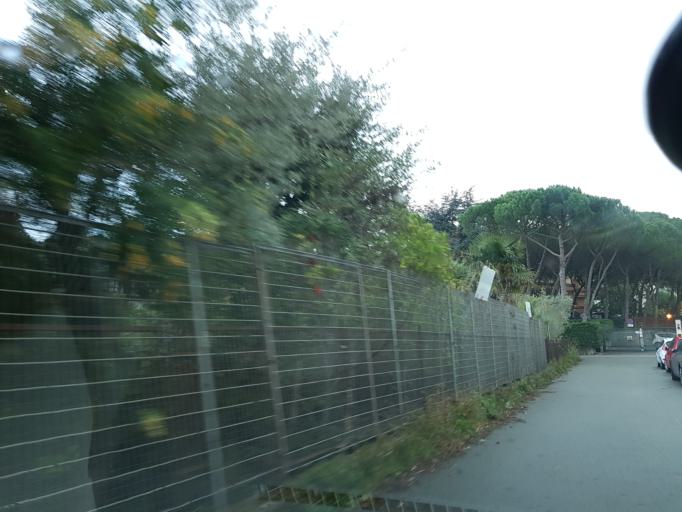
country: IT
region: Liguria
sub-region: Provincia di Genova
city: Genoa
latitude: 44.4002
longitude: 8.9711
